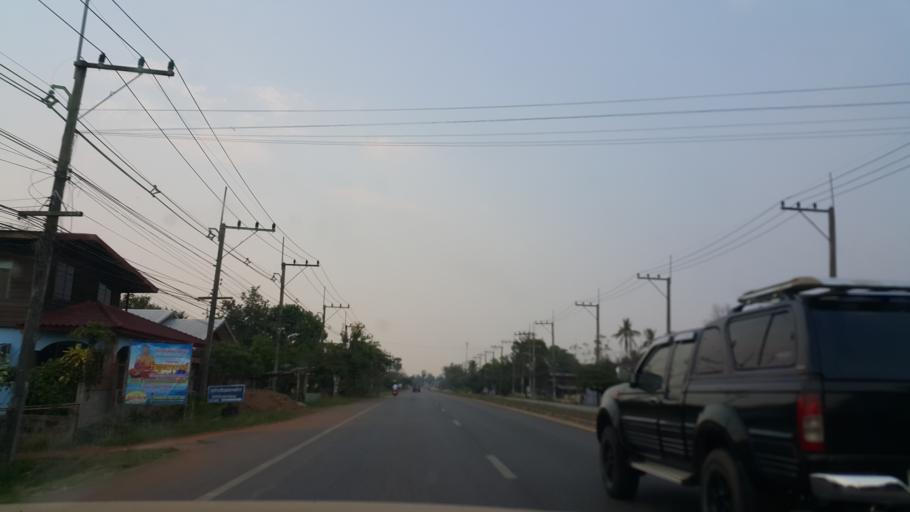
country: TH
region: Nakhon Phanom
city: That Phanom
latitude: 17.0020
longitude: 104.7232
